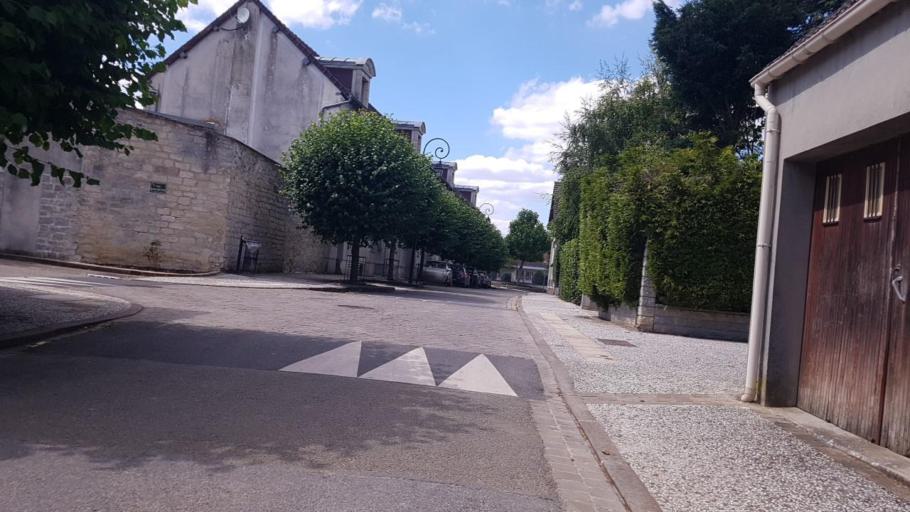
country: FR
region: Ile-de-France
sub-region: Departement de Seine-et-Marne
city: Moussy-le-Vieux
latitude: 49.0450
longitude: 2.6263
